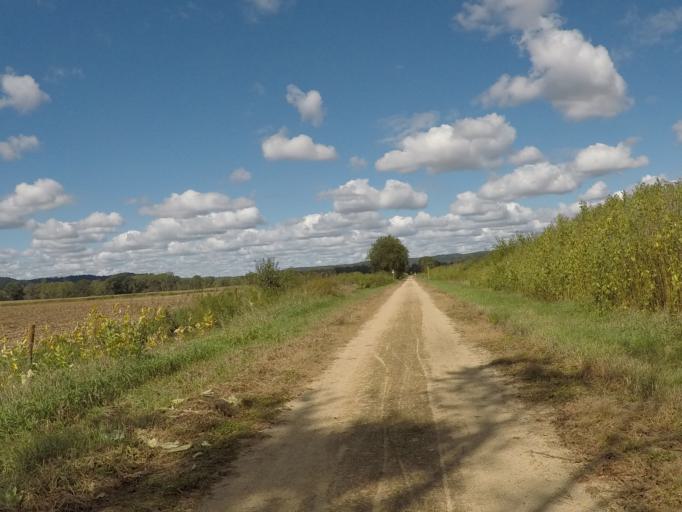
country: US
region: Wisconsin
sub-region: Richland County
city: Richland Center
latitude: 43.2936
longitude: -90.3283
